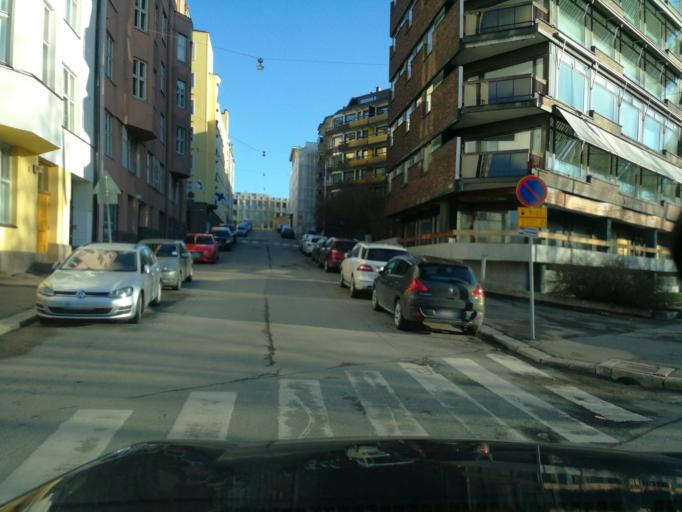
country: FI
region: Uusimaa
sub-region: Helsinki
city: Helsinki
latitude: 60.1576
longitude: 24.9530
